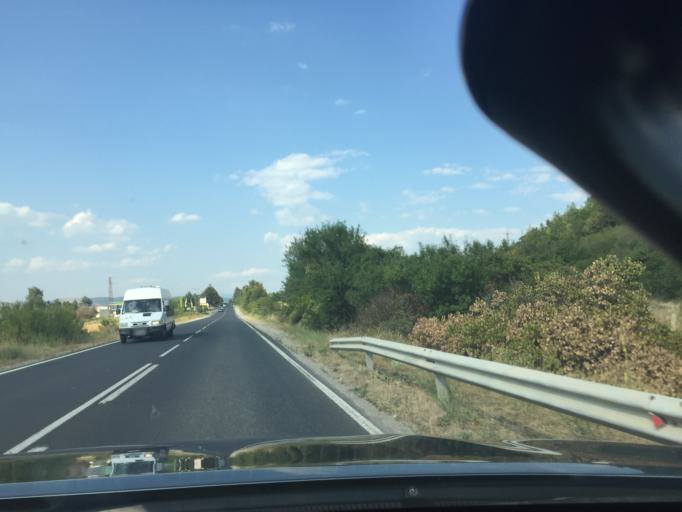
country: BG
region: Kyustendil
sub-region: Obshtina Boboshevo
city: Boboshevo
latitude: 42.2044
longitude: 23.0676
